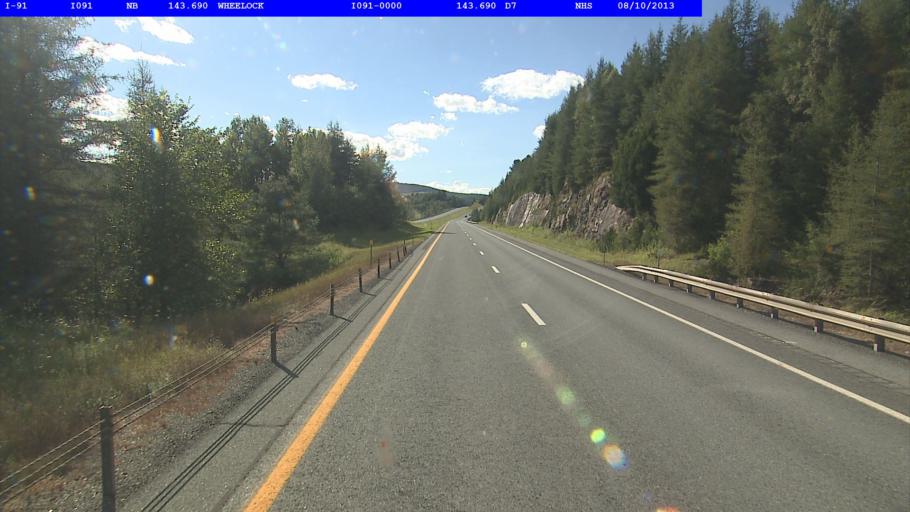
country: US
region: Vermont
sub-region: Caledonia County
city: Lyndonville
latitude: 44.5889
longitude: -72.0791
